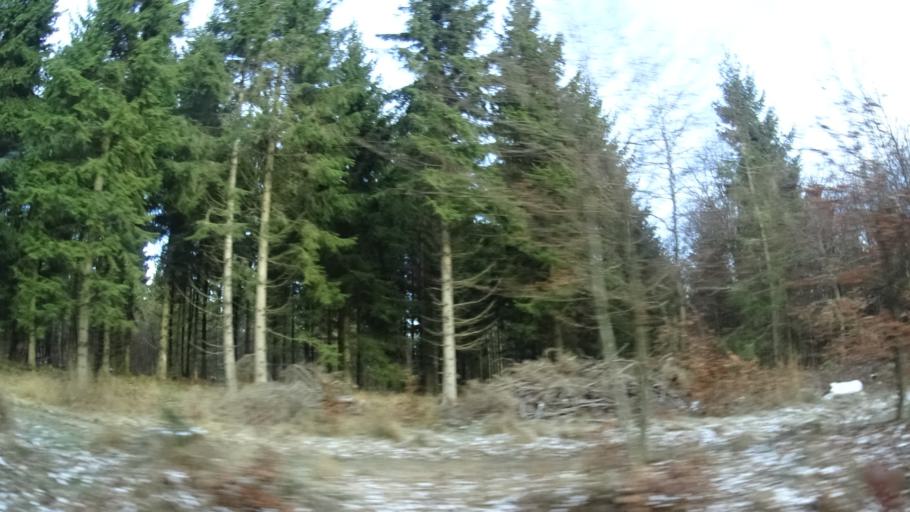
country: DE
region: Thuringia
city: Tabarz
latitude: 50.8338
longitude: 10.5242
